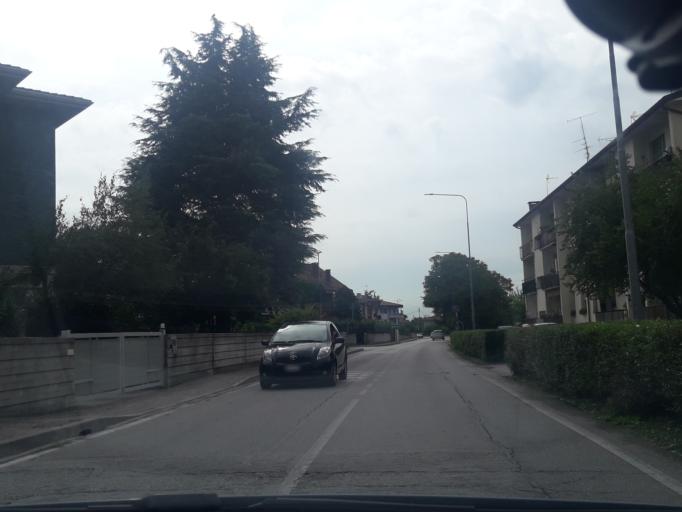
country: IT
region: Friuli Venezia Giulia
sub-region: Provincia di Udine
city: Colugna
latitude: 46.0708
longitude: 13.2138
